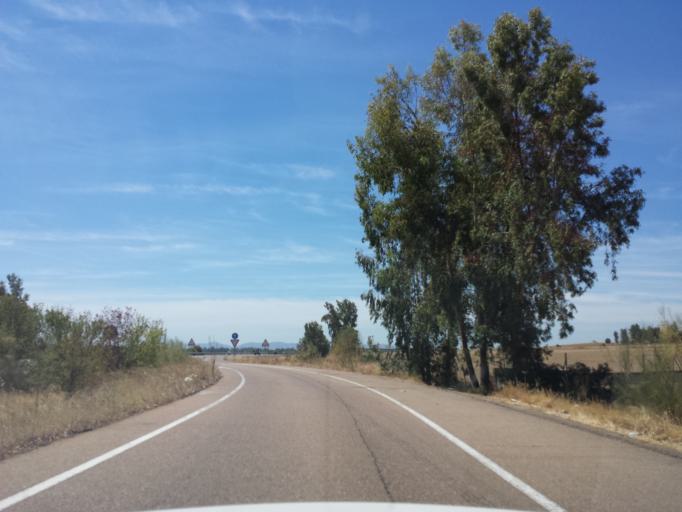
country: ES
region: Extremadura
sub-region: Provincia de Badajoz
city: Santa Amalia
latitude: 39.0036
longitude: -6.0919
